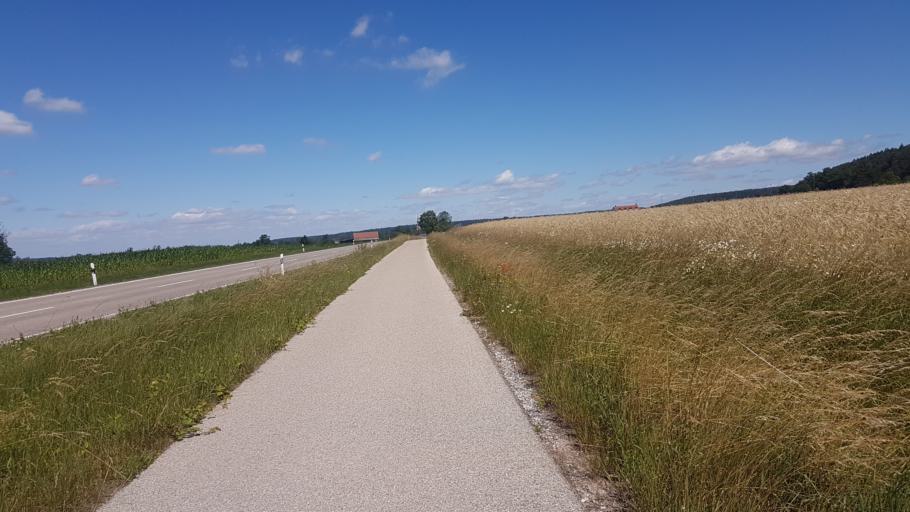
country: DE
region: Bavaria
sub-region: Regierungsbezirk Mittelfranken
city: Herrieden
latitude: 49.2503
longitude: 10.4653
